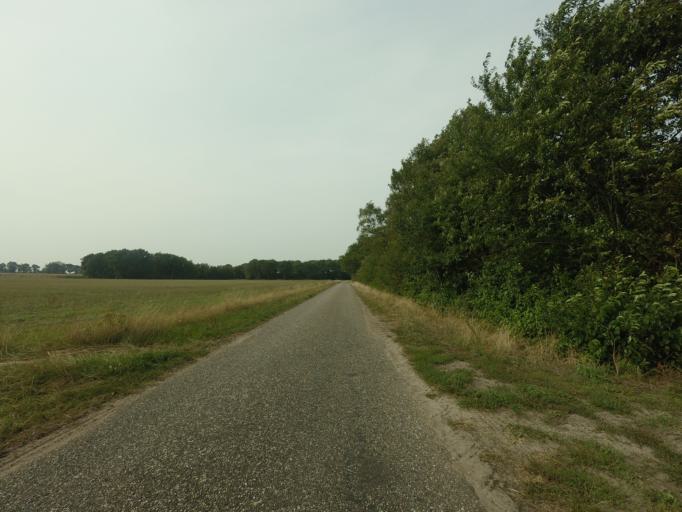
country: NL
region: Drenthe
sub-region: Gemeente Tynaarlo
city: Vries
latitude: 53.1093
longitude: 6.5444
